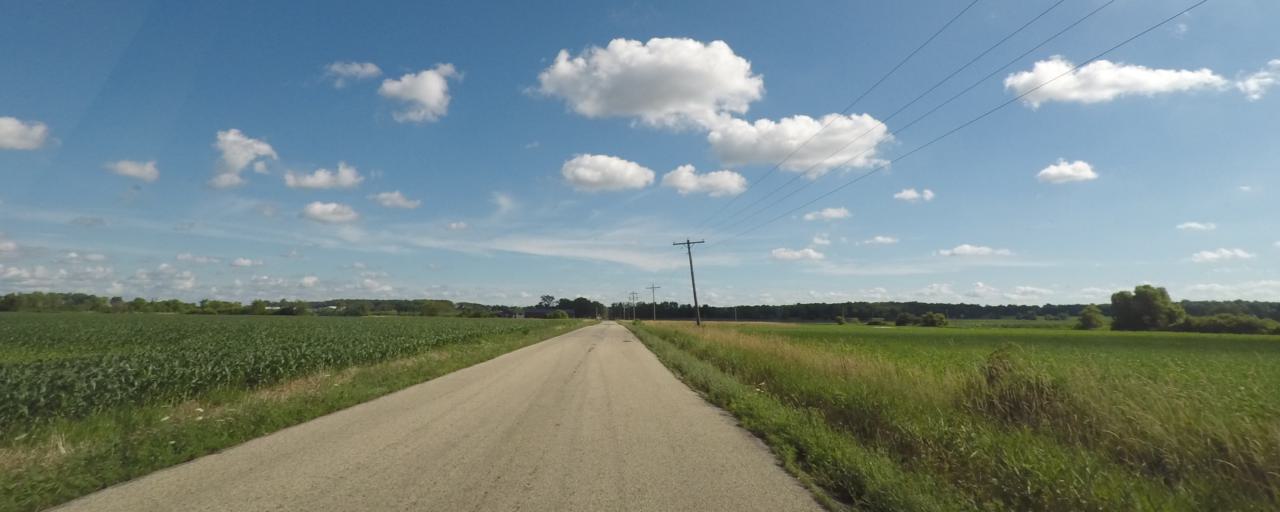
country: US
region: Wisconsin
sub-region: Rock County
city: Edgerton
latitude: 42.8433
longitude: -89.1320
